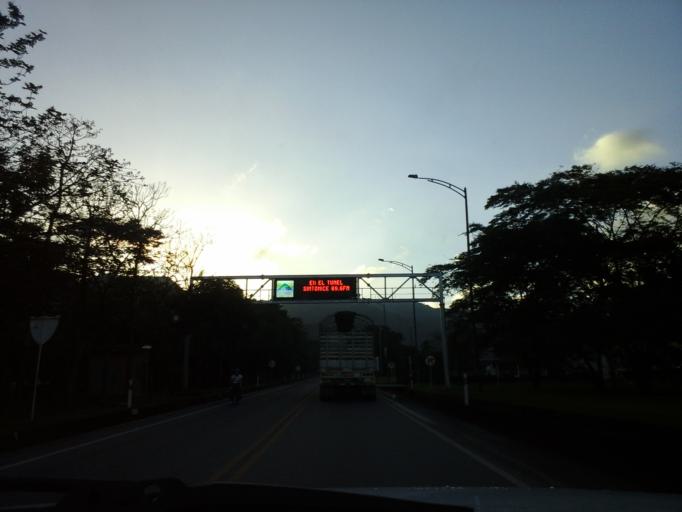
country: CO
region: Meta
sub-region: Villavicencio
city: Villavicencio
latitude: 4.1233
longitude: -73.6473
